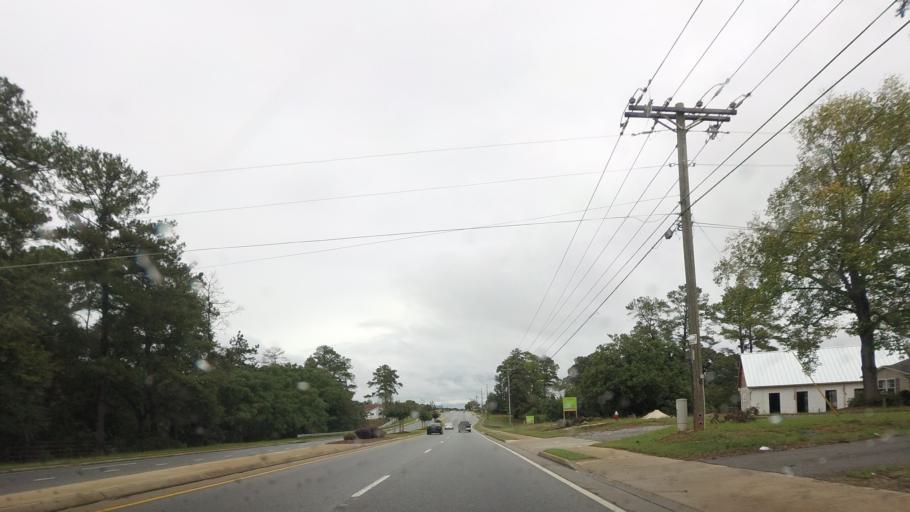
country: US
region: Georgia
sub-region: Houston County
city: Centerville
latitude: 32.5637
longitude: -83.6620
